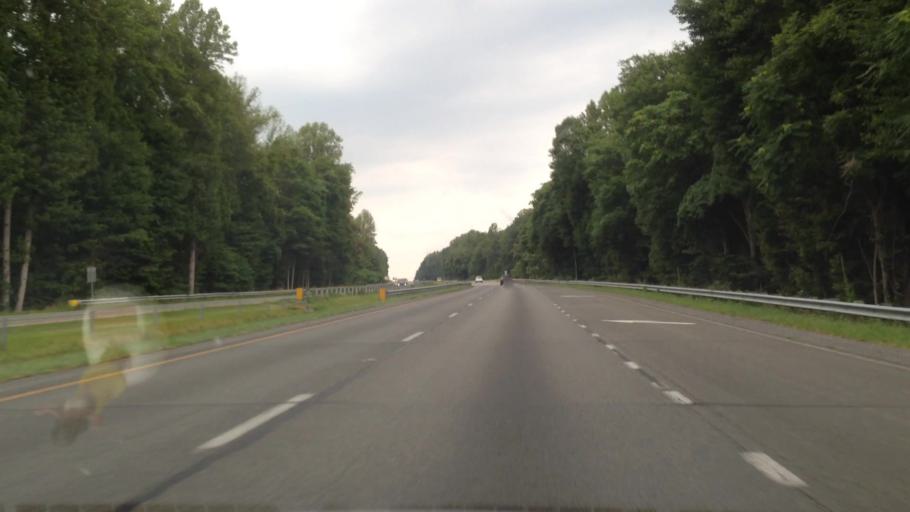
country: US
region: North Carolina
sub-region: Surry County
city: Pilot Mountain
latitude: 36.3402
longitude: -80.4581
